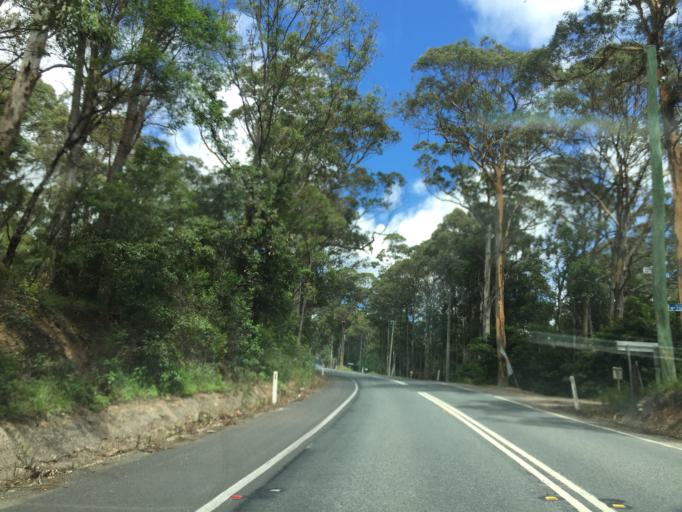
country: AU
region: New South Wales
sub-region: Hawkesbury
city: Richmond
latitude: -33.5023
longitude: 150.5380
